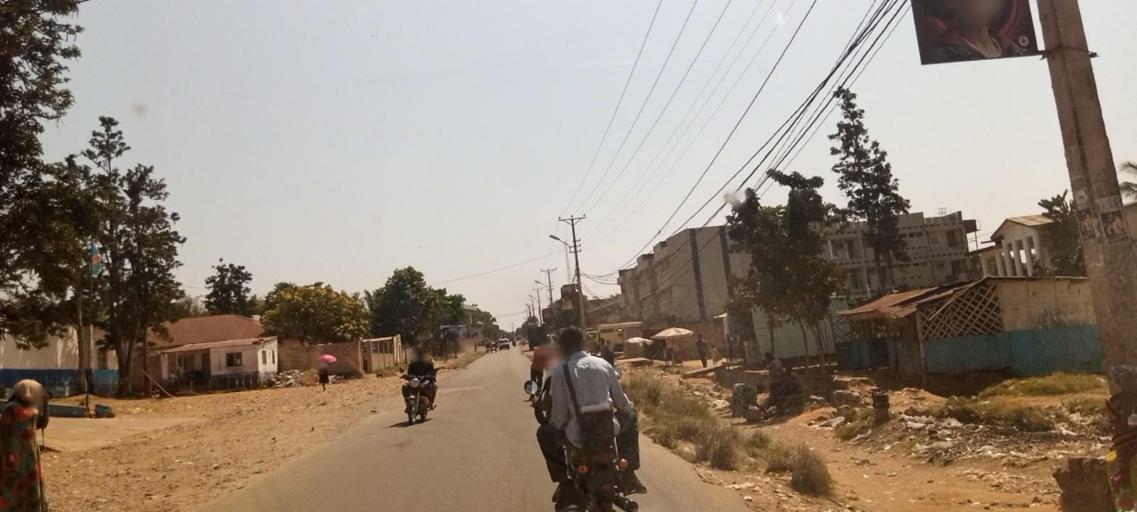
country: CD
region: Kasai-Oriental
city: Mbuji-Mayi
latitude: -6.1228
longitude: 23.5956
